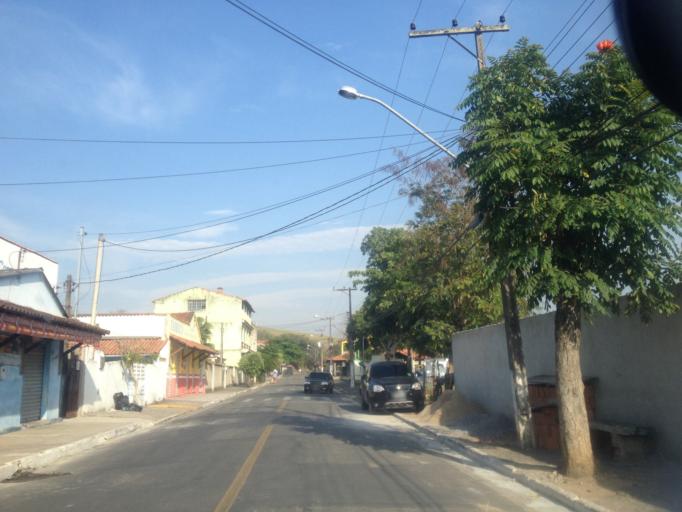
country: BR
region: Rio de Janeiro
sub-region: Porto Real
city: Porto Real
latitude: -22.4478
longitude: -44.3066
